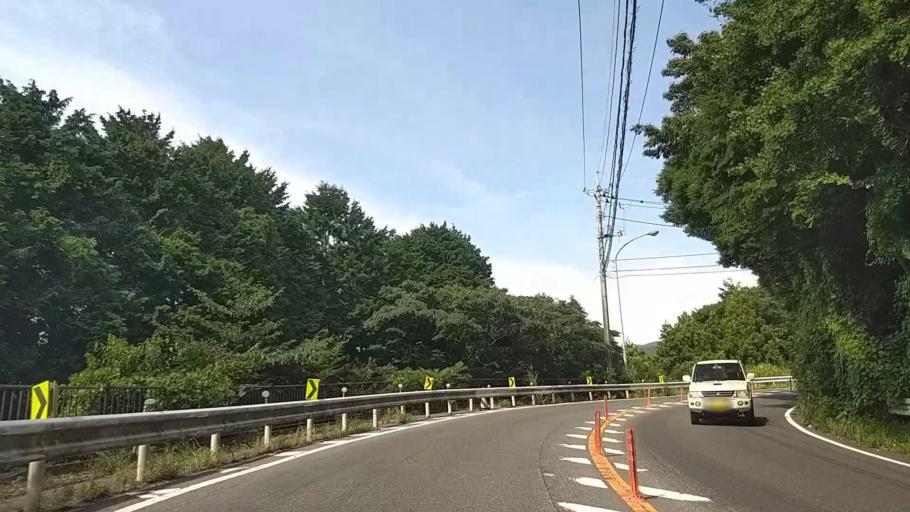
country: JP
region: Kanagawa
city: Hakone
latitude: 35.1477
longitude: 138.9777
